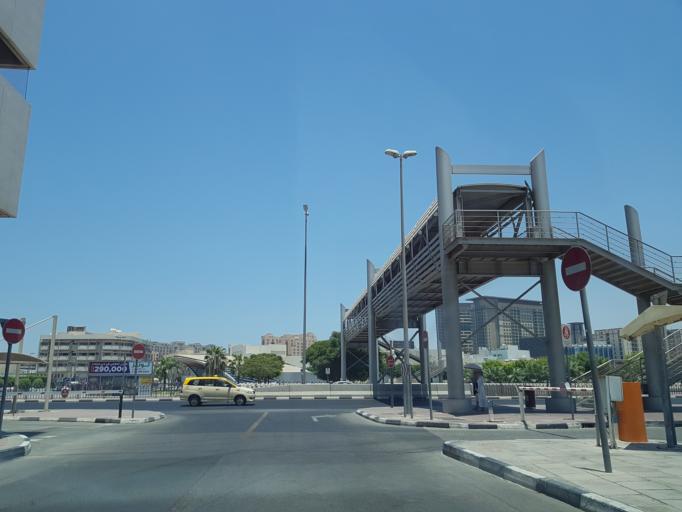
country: AE
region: Ash Shariqah
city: Sharjah
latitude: 25.2648
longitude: 55.3125
